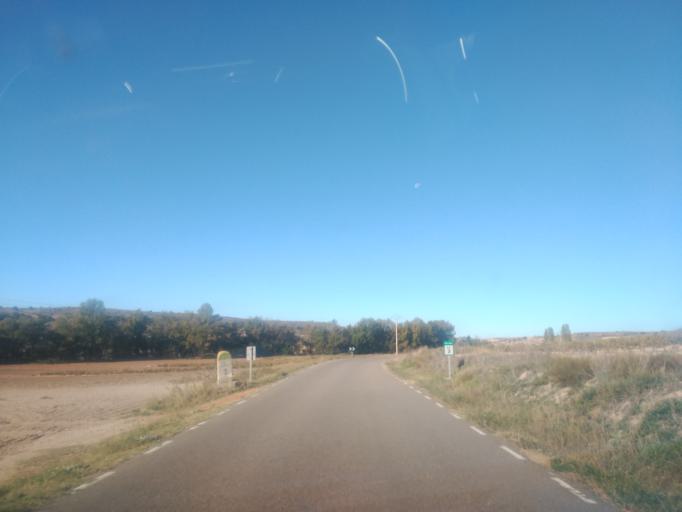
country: ES
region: Castille and Leon
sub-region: Provincia de Burgos
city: Penaranda de Duero
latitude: 41.6839
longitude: -3.4314
